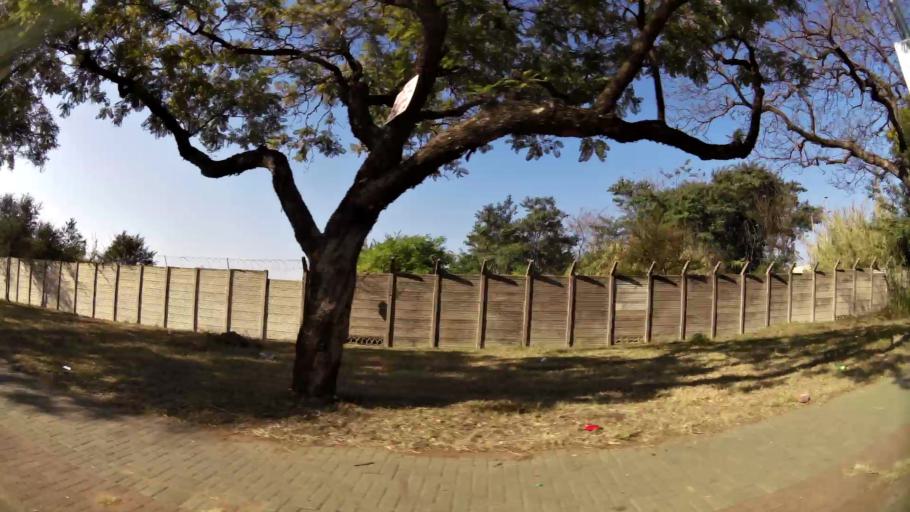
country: ZA
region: Gauteng
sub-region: City of Tshwane Metropolitan Municipality
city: Pretoria
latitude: -25.7204
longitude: 28.1866
